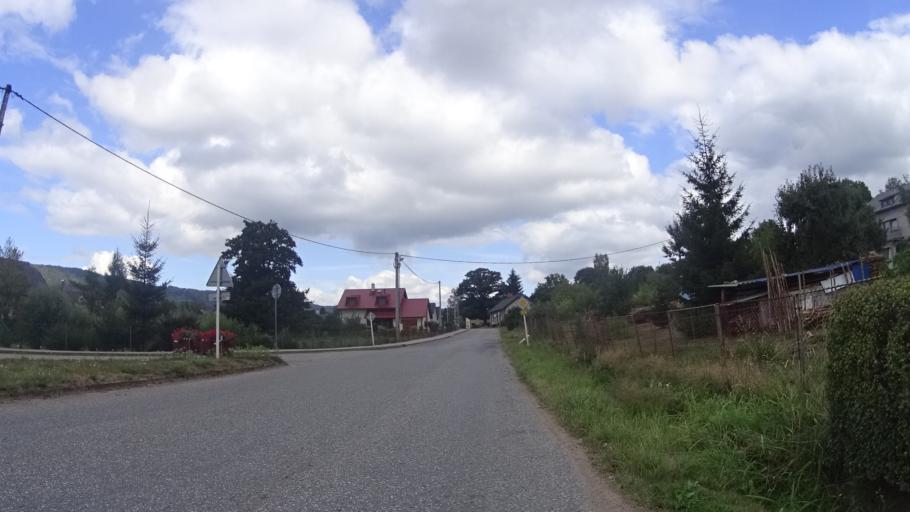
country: CZ
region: Pardubicky
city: Dolni Cermna
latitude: 49.9291
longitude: 16.5421
